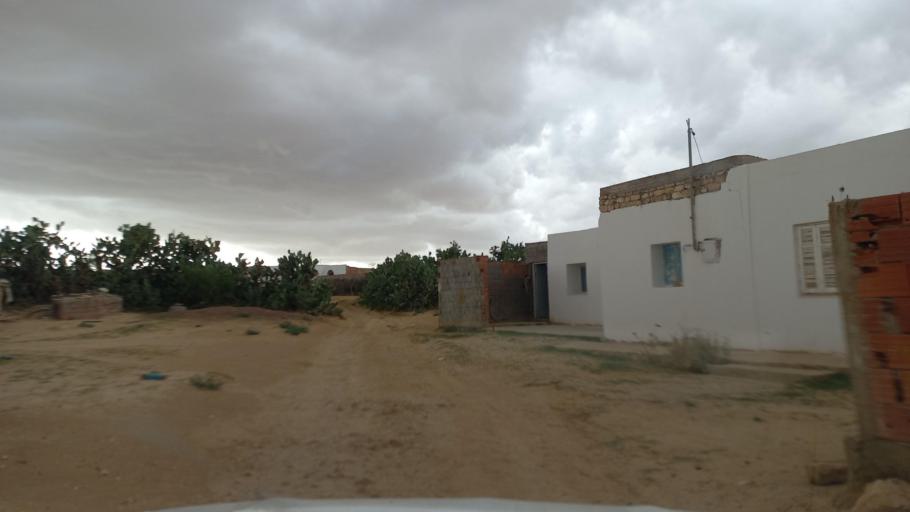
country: TN
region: Al Qasrayn
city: Kasserine
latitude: 35.2745
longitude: 8.9557
